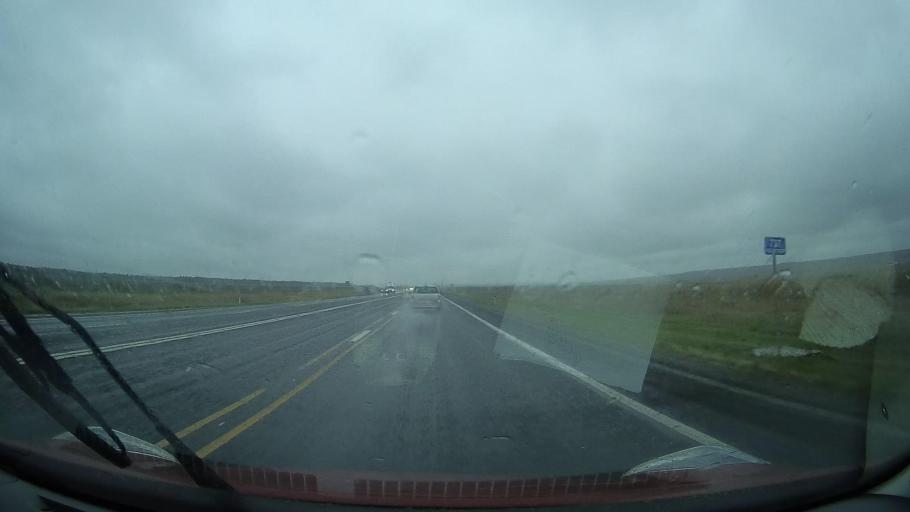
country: RU
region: Stavropol'skiy
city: Nevinnomyssk
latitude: 44.6250
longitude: 42.0619
